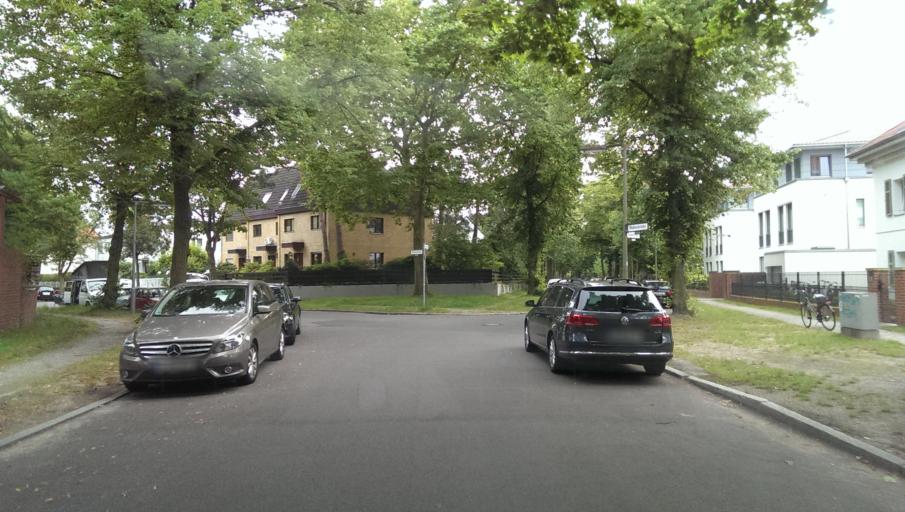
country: DE
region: Berlin
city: Zehlendorf Bezirk
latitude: 52.4495
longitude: 13.2632
